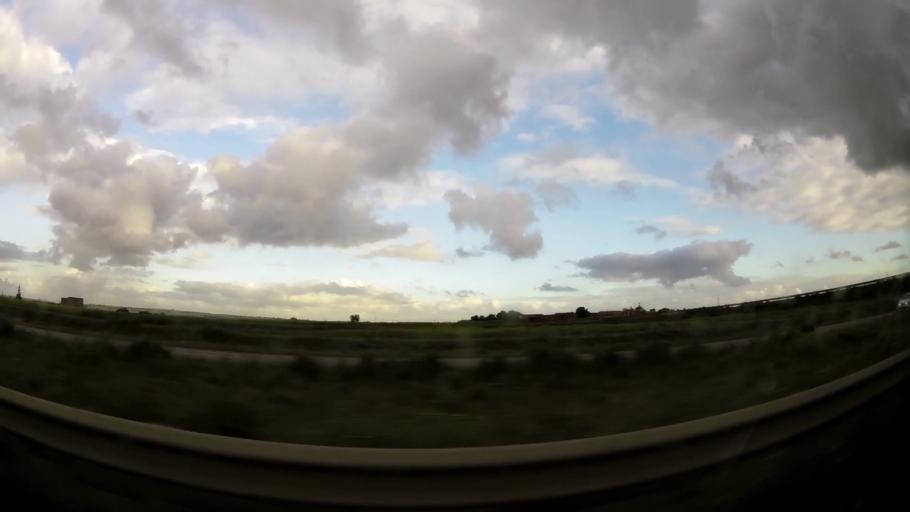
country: MA
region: Grand Casablanca
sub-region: Mediouna
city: Tit Mellil
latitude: 33.5984
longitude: -7.4408
